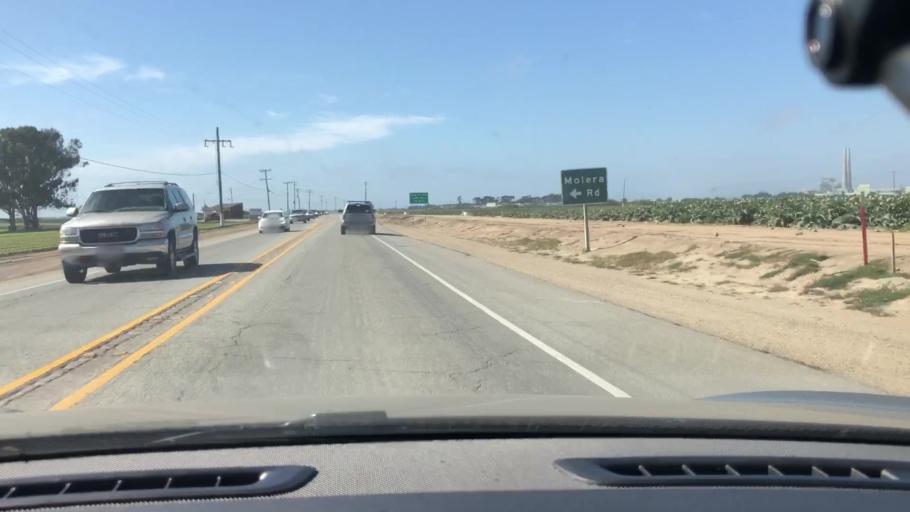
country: US
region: California
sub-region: Monterey County
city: Castroville
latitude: 36.7786
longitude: -121.7750
